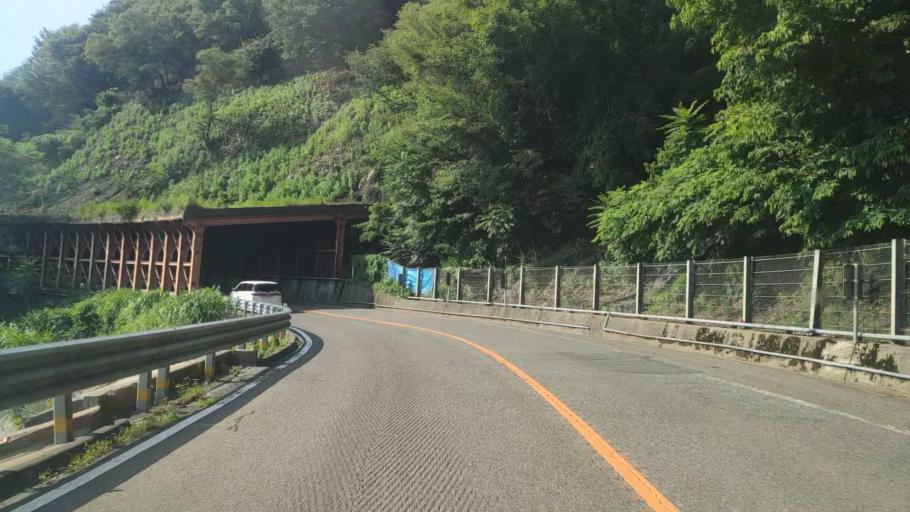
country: JP
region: Fukui
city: Takefu
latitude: 35.7902
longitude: 136.0962
